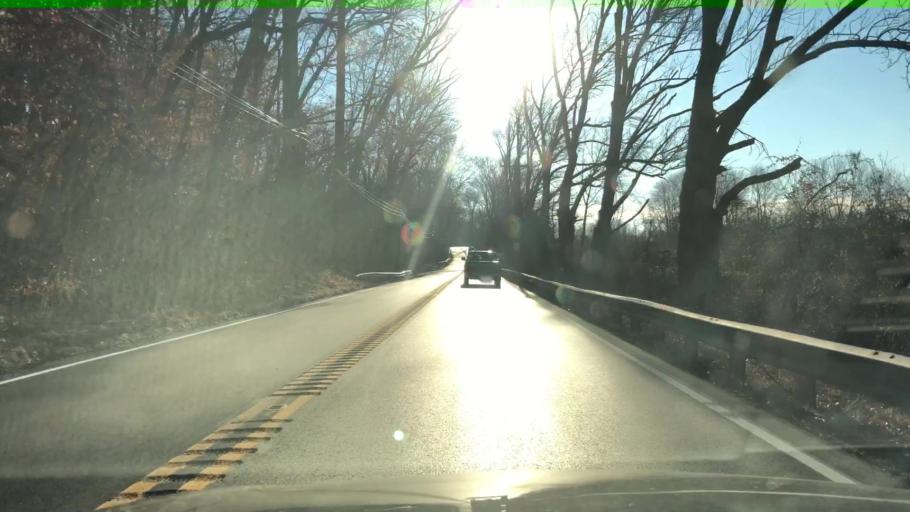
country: US
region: New Jersey
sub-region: Hunterdon County
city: Lambertville
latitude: 40.3386
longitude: -74.9329
